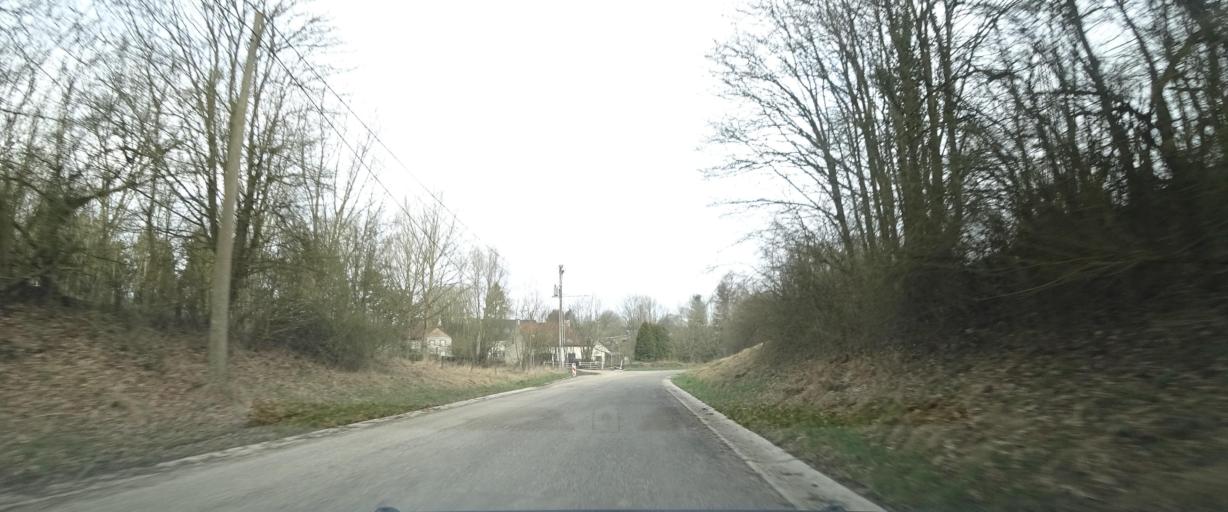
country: BE
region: Wallonia
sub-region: Province de Namur
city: Sombreffe
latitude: 50.4939
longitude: 4.6289
